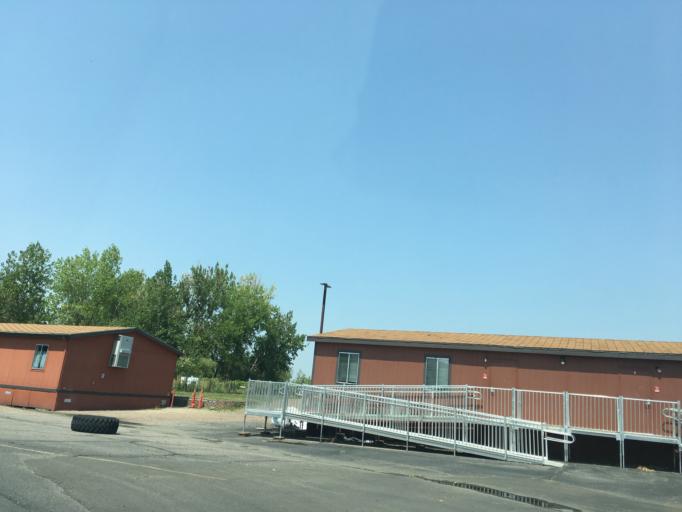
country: US
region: Colorado
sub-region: Adams County
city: Aurora
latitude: 39.7128
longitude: -104.8594
